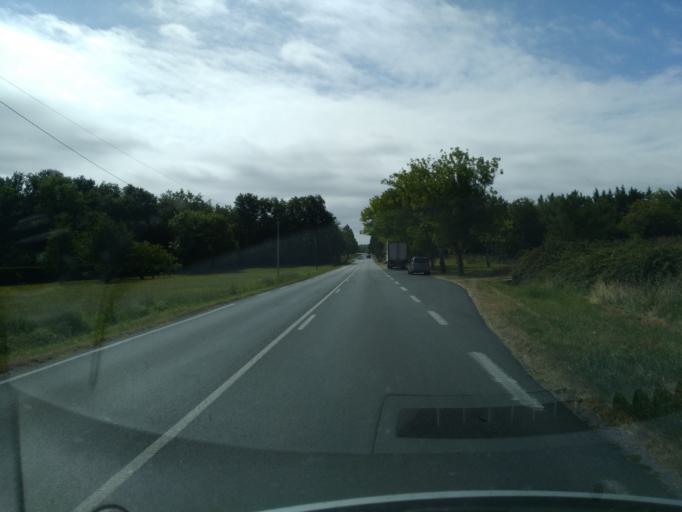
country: FR
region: Poitou-Charentes
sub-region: Departement de la Charente-Maritime
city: Chaillevette
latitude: 45.7141
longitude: -1.0675
